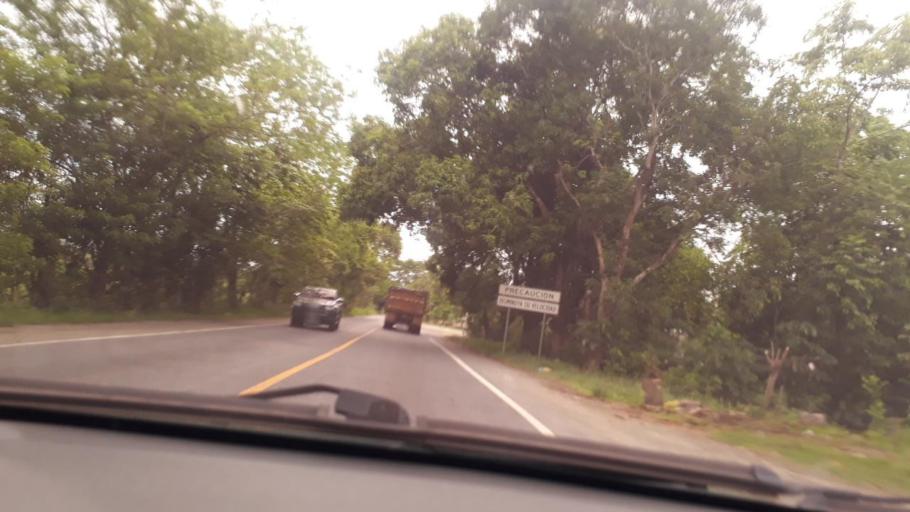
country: GT
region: Izabal
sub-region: Municipio de Los Amates
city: Los Amates
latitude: 15.3164
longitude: -89.0488
